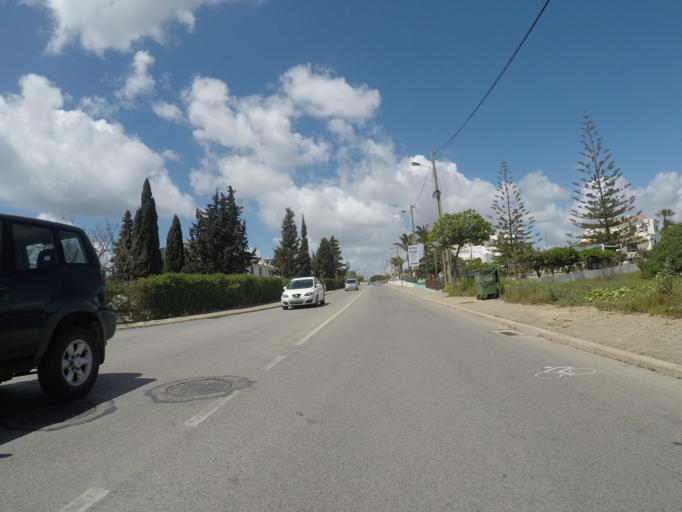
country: PT
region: Faro
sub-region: Silves
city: Armacao de Pera
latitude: 37.1058
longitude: -8.3800
